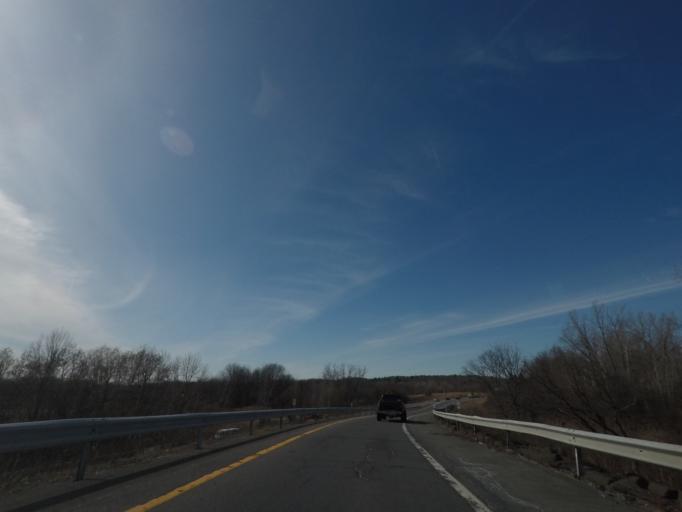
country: US
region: New York
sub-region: Albany County
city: Cohoes
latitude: 42.7635
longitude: -73.7588
